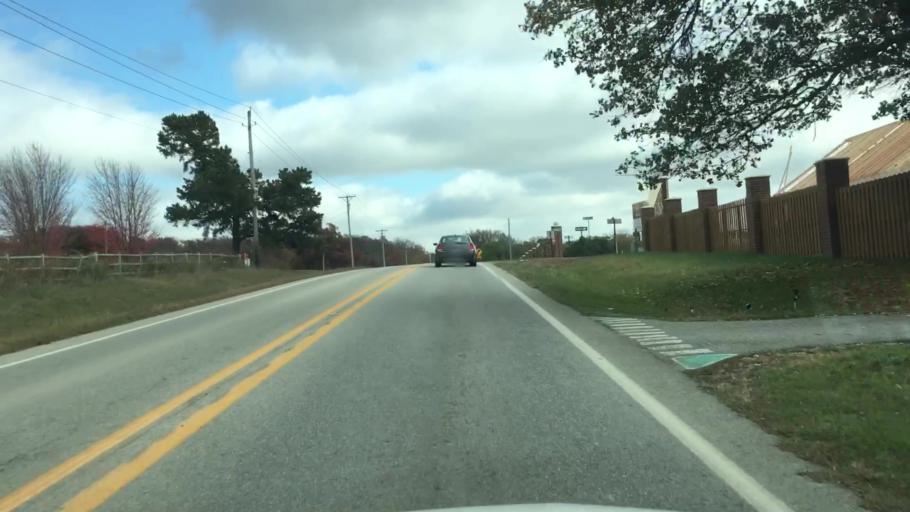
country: US
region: Arkansas
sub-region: Benton County
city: Gentry
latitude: 36.2633
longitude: -94.4558
